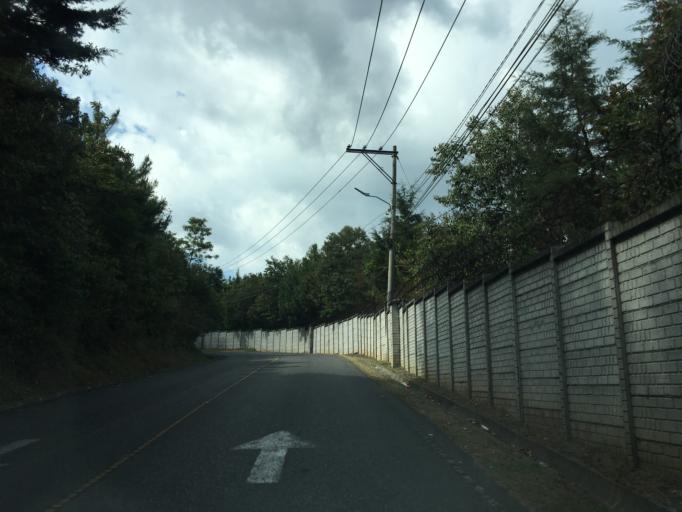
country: GT
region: Guatemala
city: San Jose Pinula
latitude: 14.5568
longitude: -90.4533
